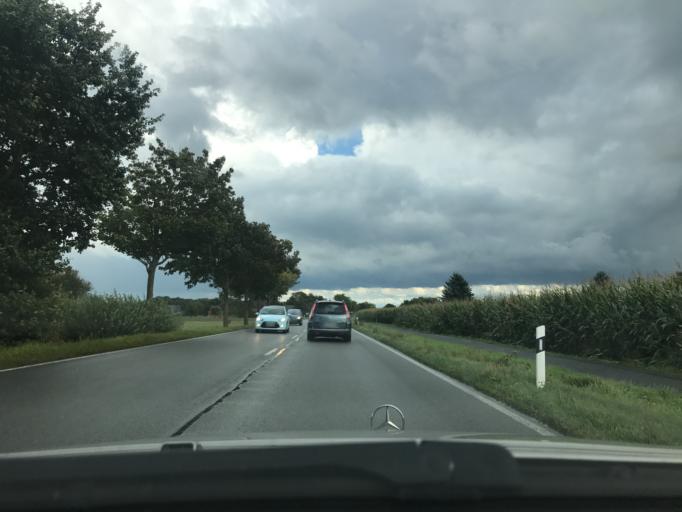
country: DE
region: North Rhine-Westphalia
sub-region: Regierungsbezirk Arnsberg
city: Soest
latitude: 51.6498
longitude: 8.0743
